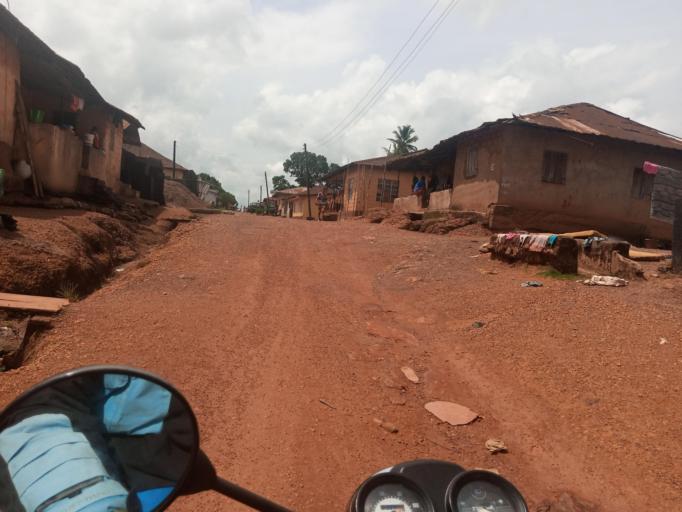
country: SL
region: Southern Province
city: Bo
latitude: 7.9694
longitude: -11.7366
